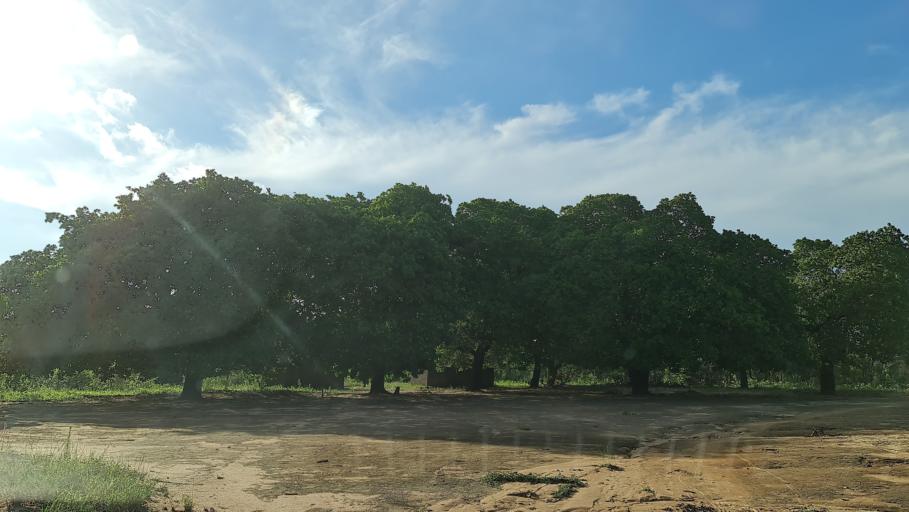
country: MZ
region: Zambezia
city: Quelimane
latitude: -17.1914
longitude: 37.4128
